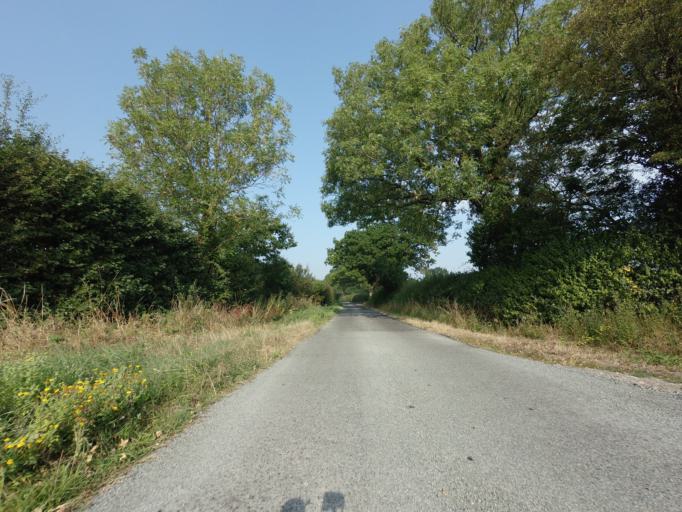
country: GB
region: England
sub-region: Kent
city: Headcorn
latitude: 51.1283
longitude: 0.6575
